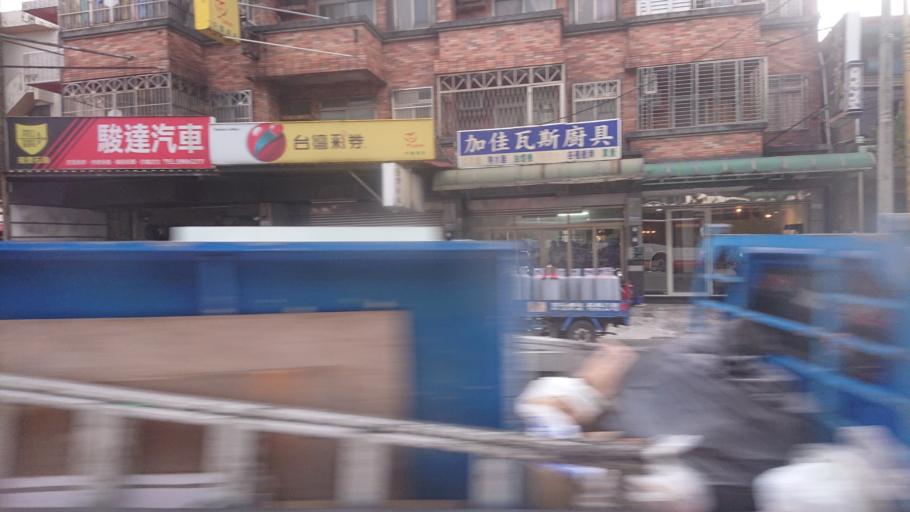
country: TW
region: Taiwan
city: Daxi
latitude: 24.8863
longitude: 121.2699
